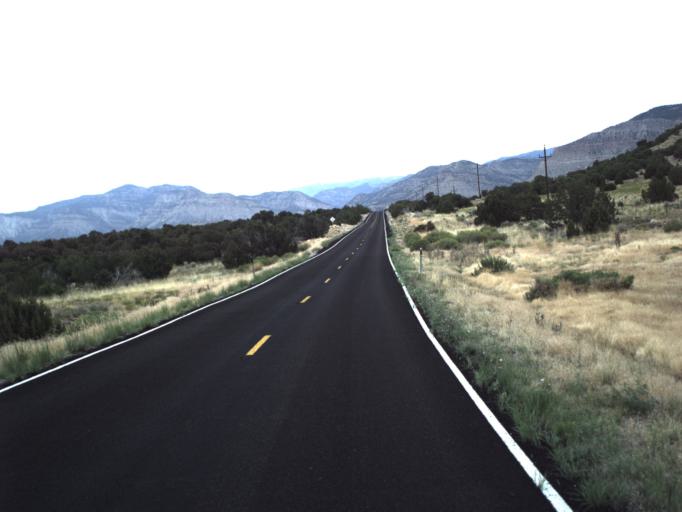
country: US
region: Utah
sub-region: Carbon County
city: East Carbon City
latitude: 39.4902
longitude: -110.4042
